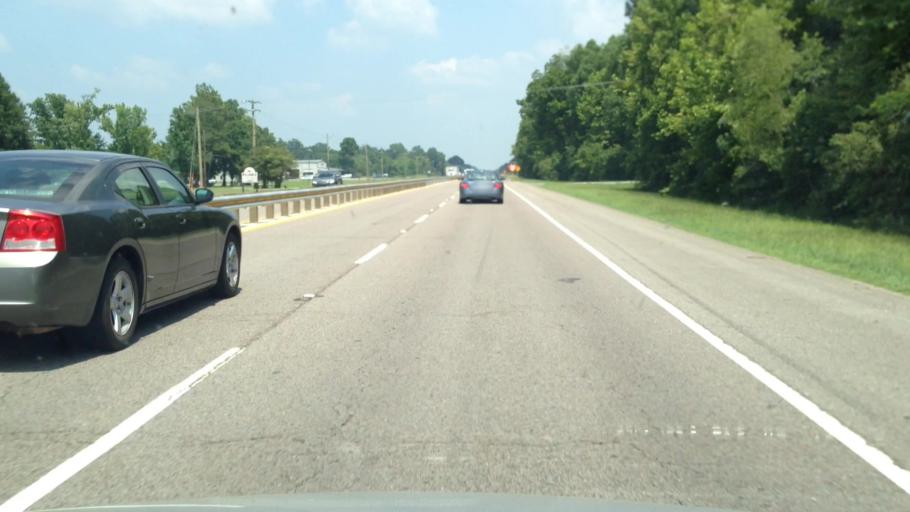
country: US
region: Louisiana
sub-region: Pointe Coupee Parish
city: Livonia
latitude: 30.5541
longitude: -91.5323
